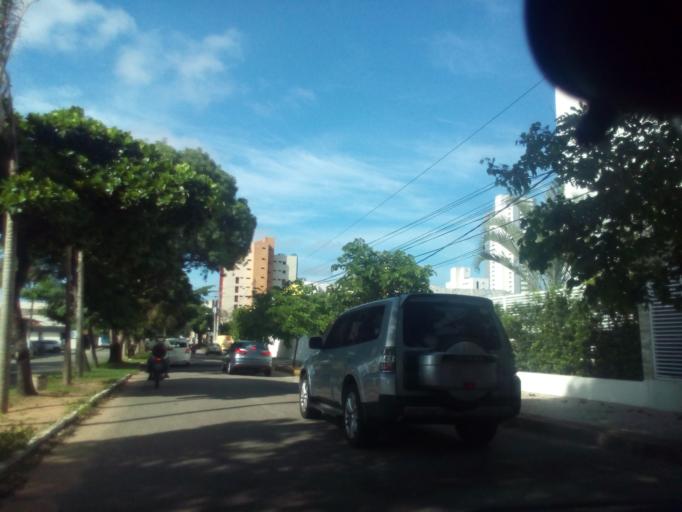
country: BR
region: Rio Grande do Norte
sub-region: Natal
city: Natal
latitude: -5.8201
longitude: -35.2154
